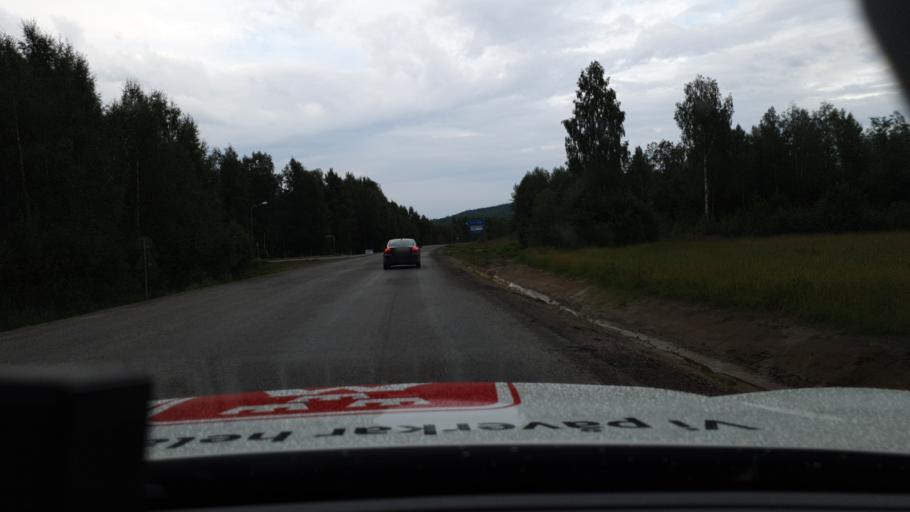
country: SE
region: Norrbotten
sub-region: Bodens Kommun
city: Boden
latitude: 65.8511
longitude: 21.5683
